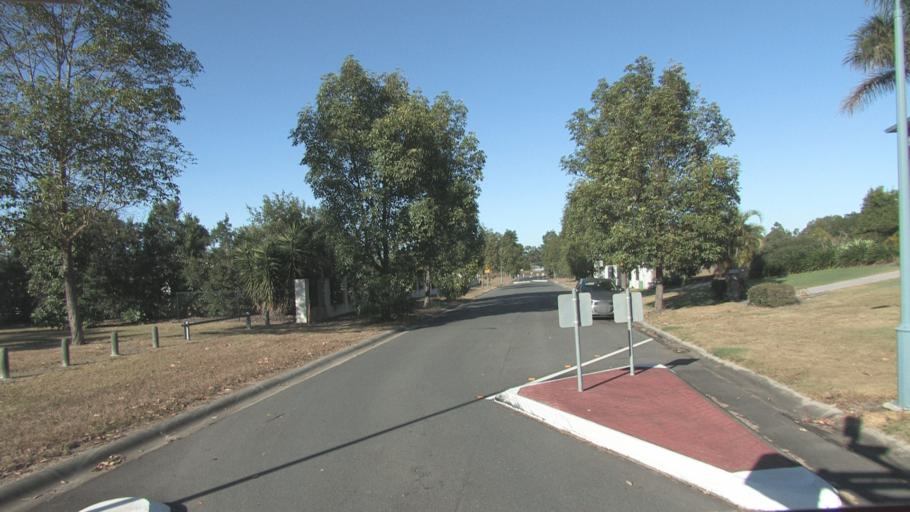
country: AU
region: Queensland
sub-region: Brisbane
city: Forest Lake
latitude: -27.6542
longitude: 152.9880
